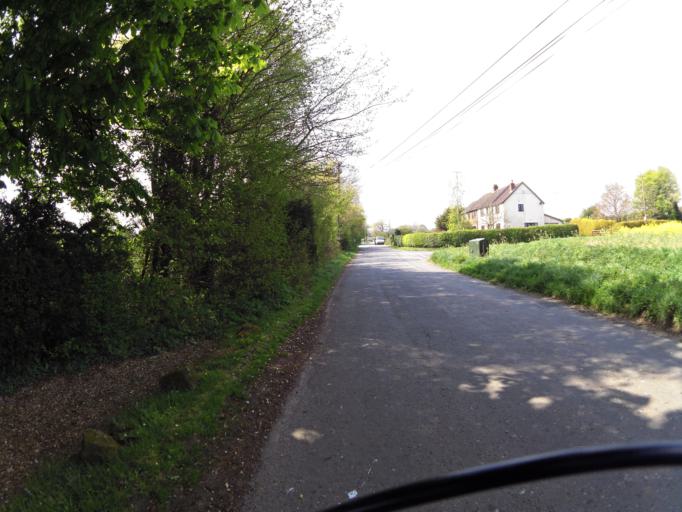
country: GB
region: England
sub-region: Suffolk
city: Hadleigh
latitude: 52.0826
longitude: 1.0049
